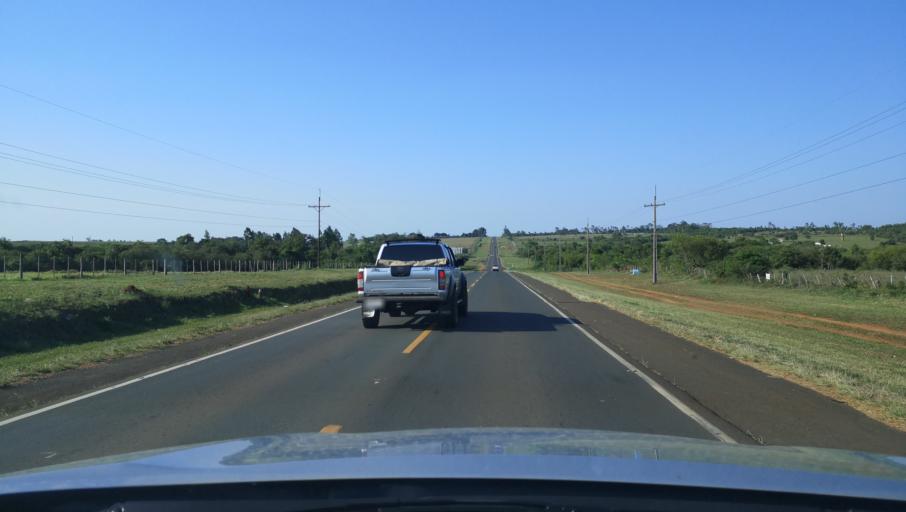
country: PY
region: Misiones
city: Santa Maria
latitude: -26.8361
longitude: -57.0339
